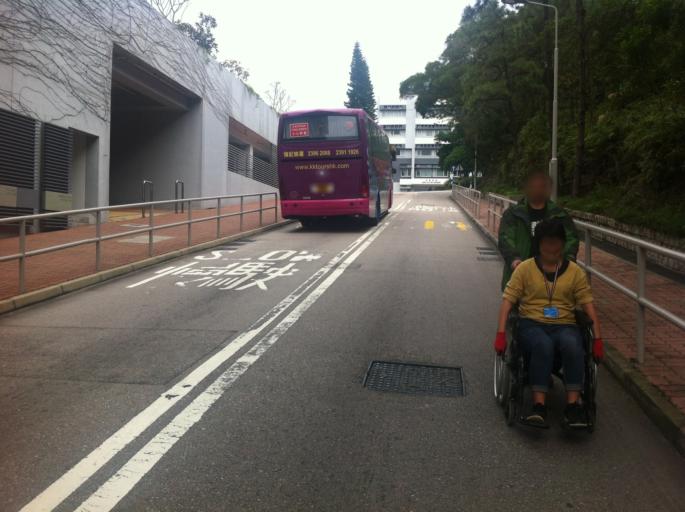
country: HK
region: Sha Tin
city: Sha Tin
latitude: 22.4199
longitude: 114.2039
